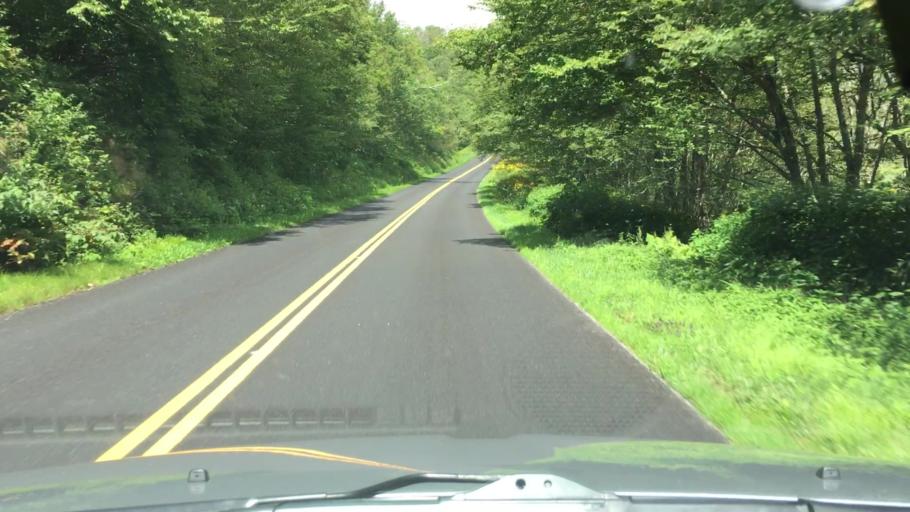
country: US
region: North Carolina
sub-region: Buncombe County
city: Black Mountain
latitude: 35.7374
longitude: -82.3425
